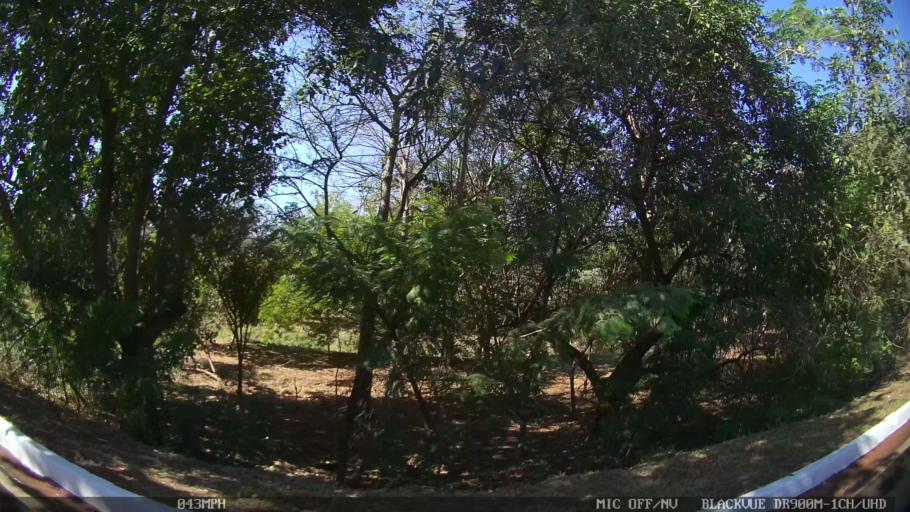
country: BR
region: Sao Paulo
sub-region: Ribeirao Preto
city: Ribeirao Preto
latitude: -21.2293
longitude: -47.7670
